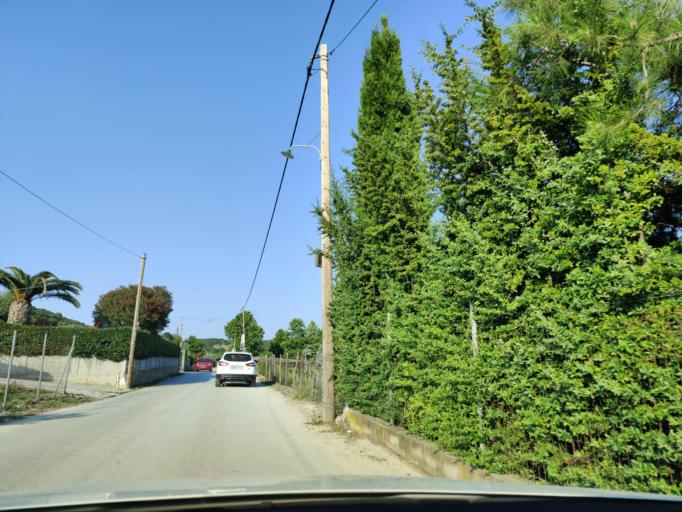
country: GR
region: East Macedonia and Thrace
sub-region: Nomos Kavalas
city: Nea Peramos
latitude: 40.8175
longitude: 24.3016
